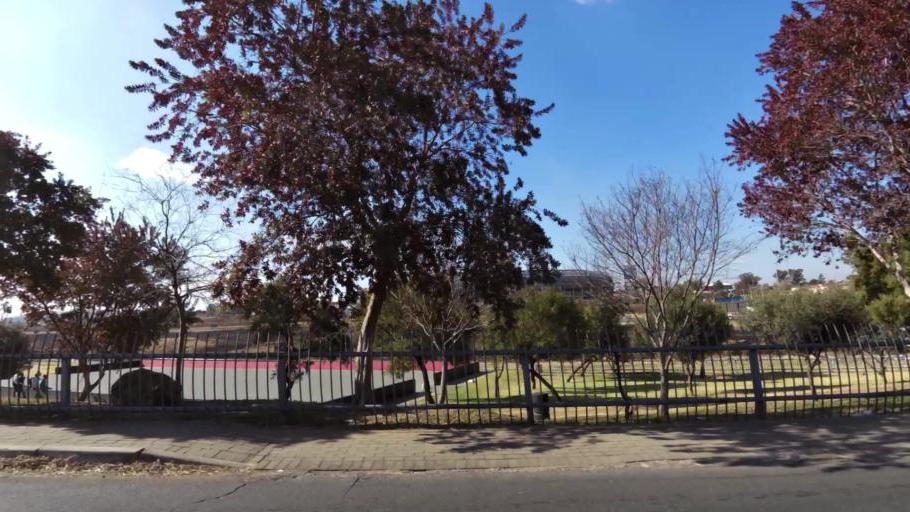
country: ZA
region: Gauteng
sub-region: City of Johannesburg Metropolitan Municipality
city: Soweto
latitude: -26.2296
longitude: 27.9190
